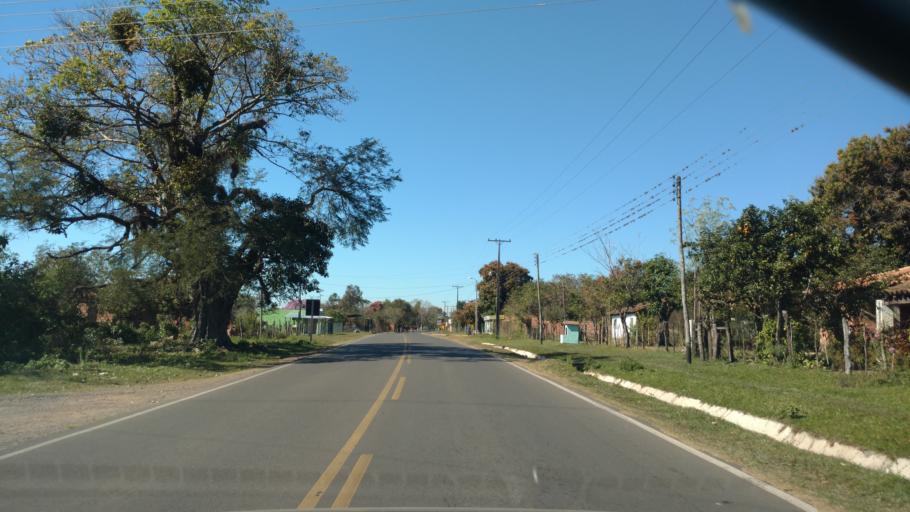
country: PY
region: Central
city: Ypacarai
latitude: -25.4234
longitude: -57.2929
